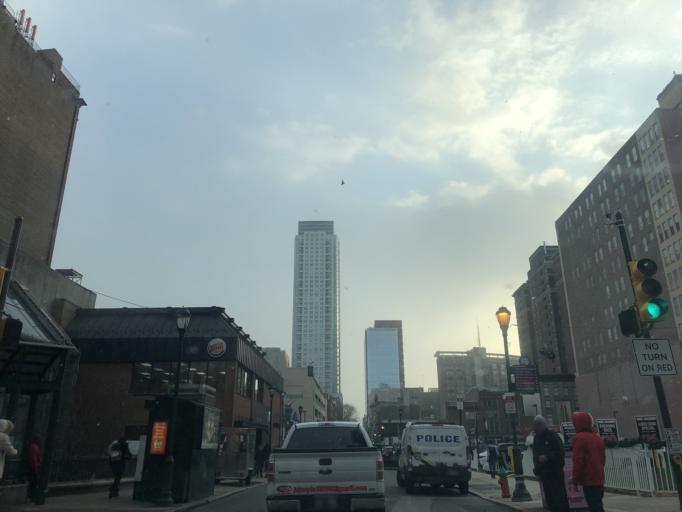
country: US
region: Pennsylvania
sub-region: Philadelphia County
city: Philadelphia
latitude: 39.9511
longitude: -75.1536
